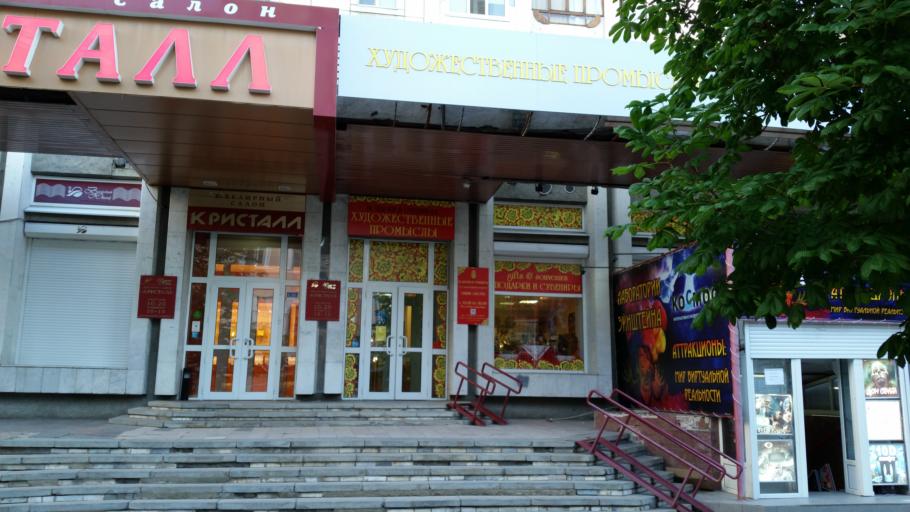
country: RU
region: Saratov
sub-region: Saratovskiy Rayon
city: Saratov
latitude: 51.5307
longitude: 46.0315
